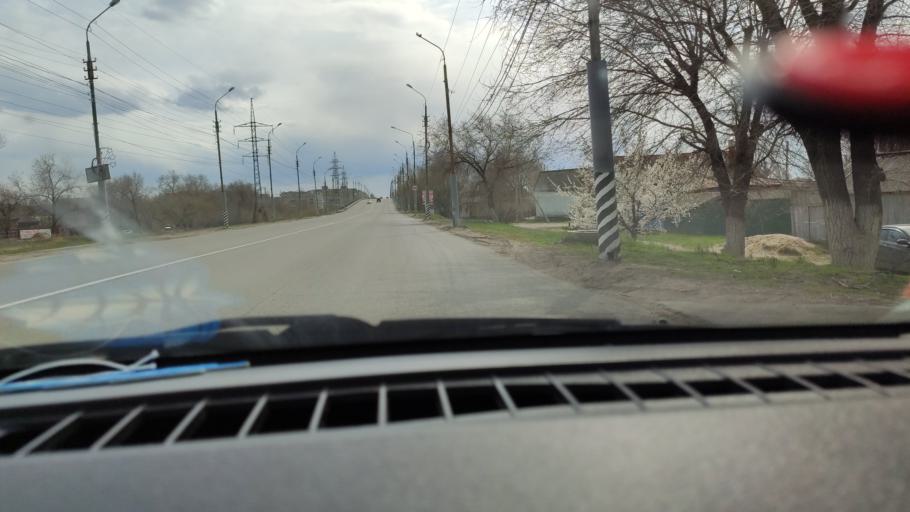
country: RU
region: Saratov
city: Privolzhskiy
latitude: 51.4167
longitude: 46.0451
